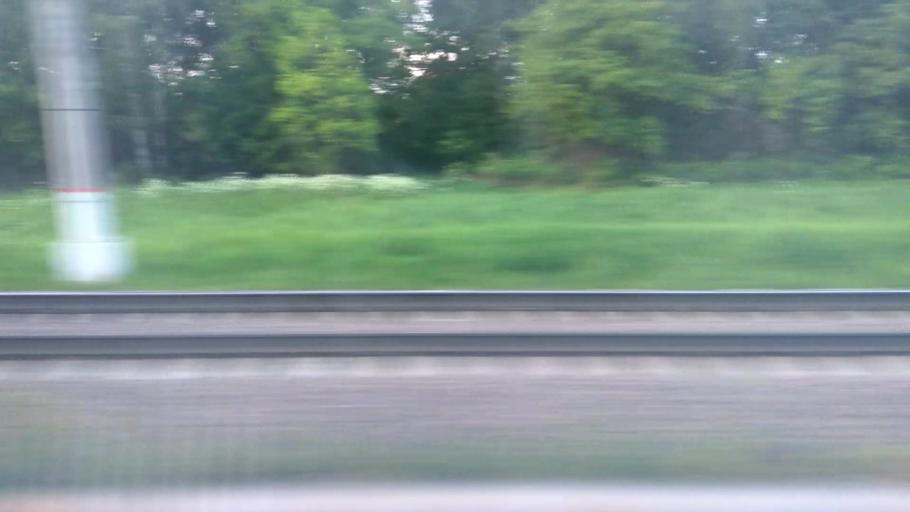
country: RU
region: Moskovskaya
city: Vostryakovo
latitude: 55.3789
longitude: 37.8173
